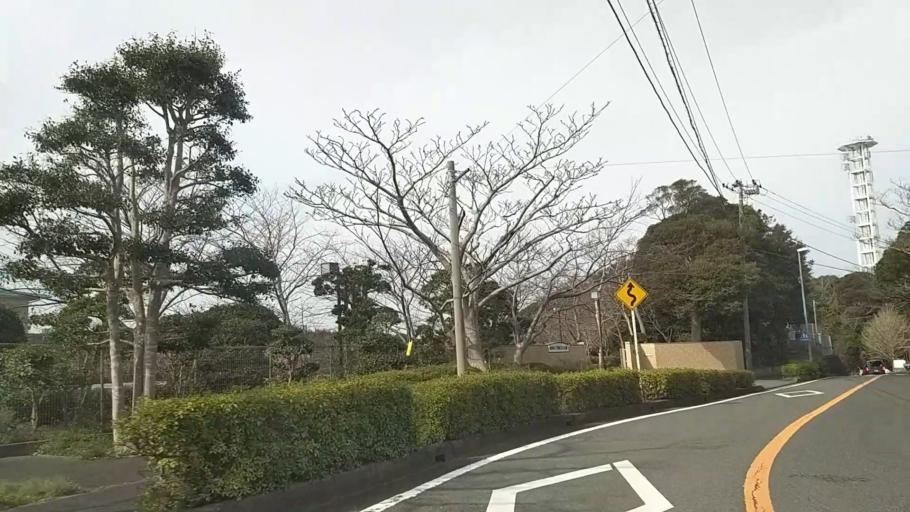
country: JP
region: Shizuoka
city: Shimoda
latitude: 34.6645
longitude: 138.9673
